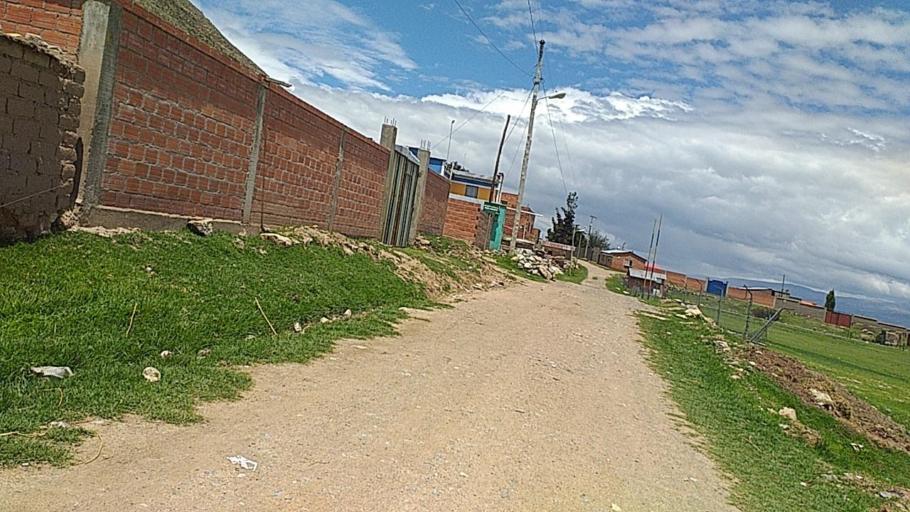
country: BO
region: La Paz
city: Huatajata
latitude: -16.3137
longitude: -68.6754
